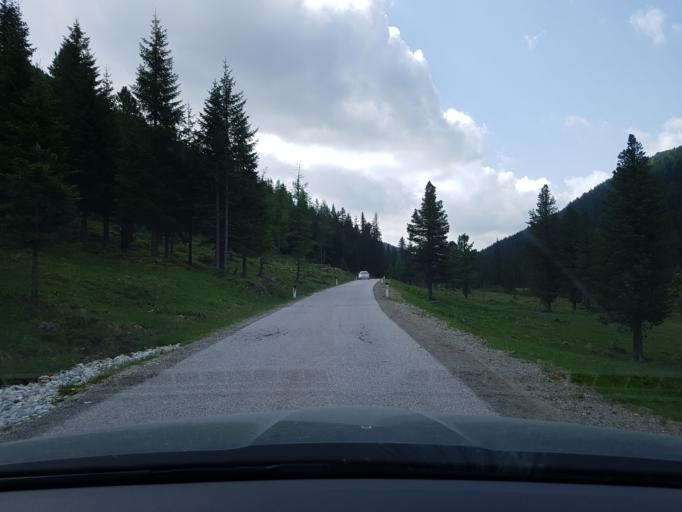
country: AT
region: Salzburg
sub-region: Politischer Bezirk Tamsweg
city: Thomatal
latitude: 47.0258
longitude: 13.7619
